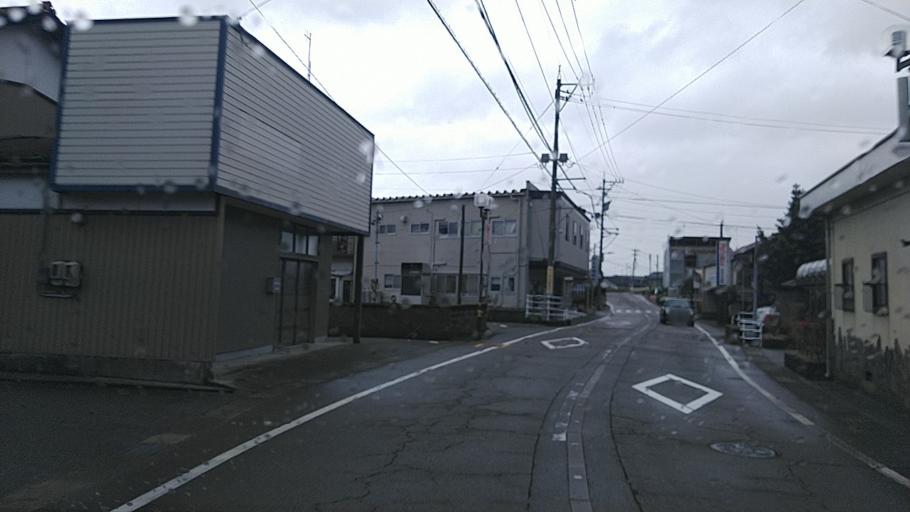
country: JP
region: Ishikawa
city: Komatsu
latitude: 36.3283
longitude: 136.3868
